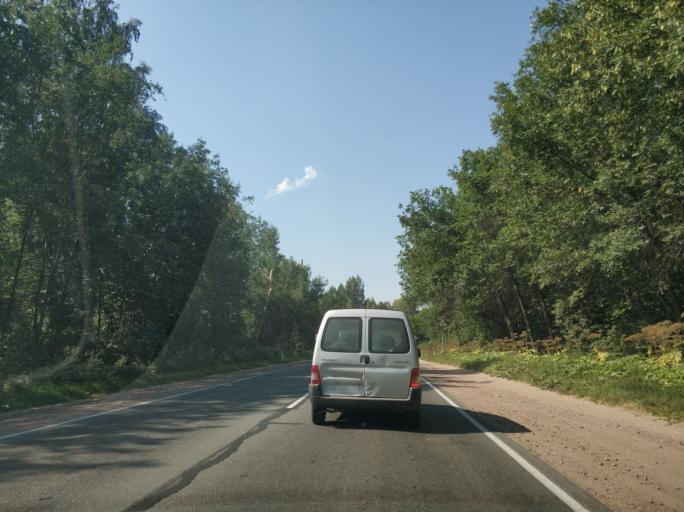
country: RU
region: Leningrad
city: Vsevolozhsk
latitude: 60.0397
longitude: 30.6705
